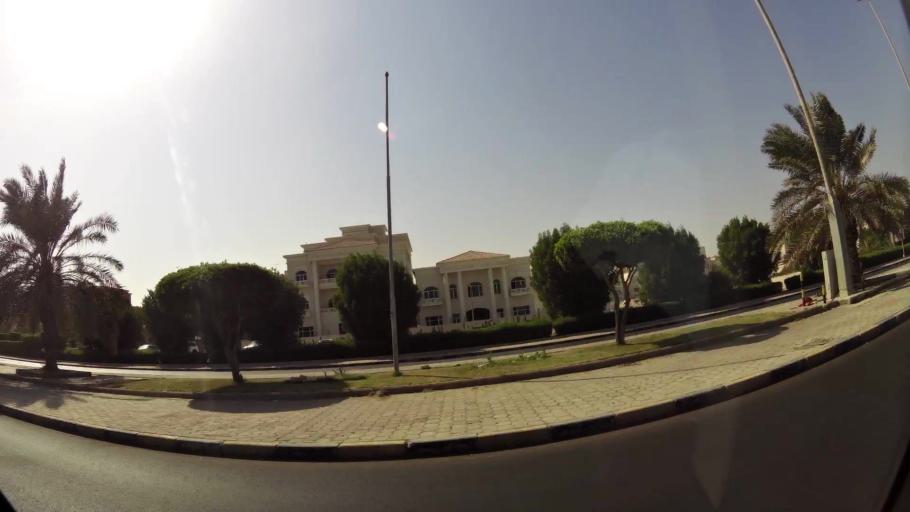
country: KW
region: Muhafazat Hawalli
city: Salwa
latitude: 29.2753
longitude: 48.0890
